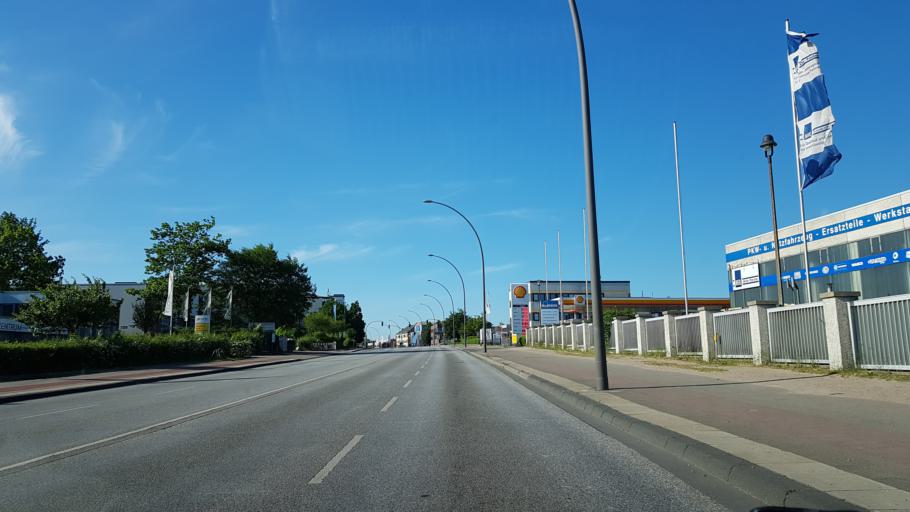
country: DE
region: Hamburg
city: Stellingen
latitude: 53.5725
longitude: 9.9187
